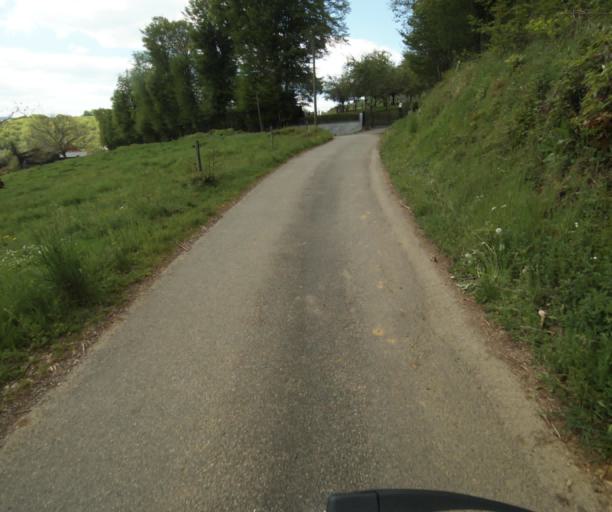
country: FR
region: Limousin
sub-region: Departement de la Correze
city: Naves
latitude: 45.2916
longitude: 1.7650
